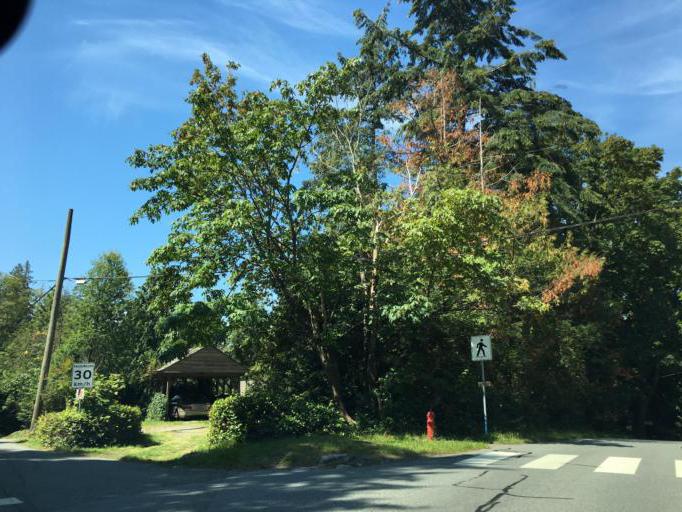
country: CA
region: British Columbia
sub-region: Greater Vancouver Regional District
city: Bowen Island
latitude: 49.3407
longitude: -123.2631
